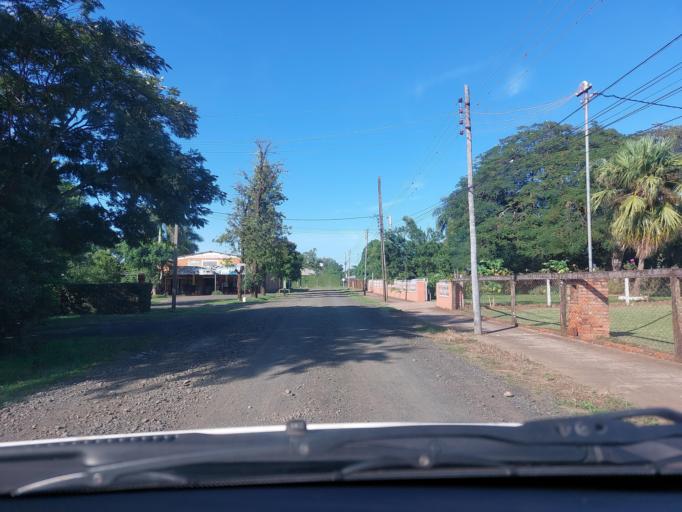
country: PY
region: San Pedro
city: Itacurubi del Rosario
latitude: -24.6115
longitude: -56.7951
